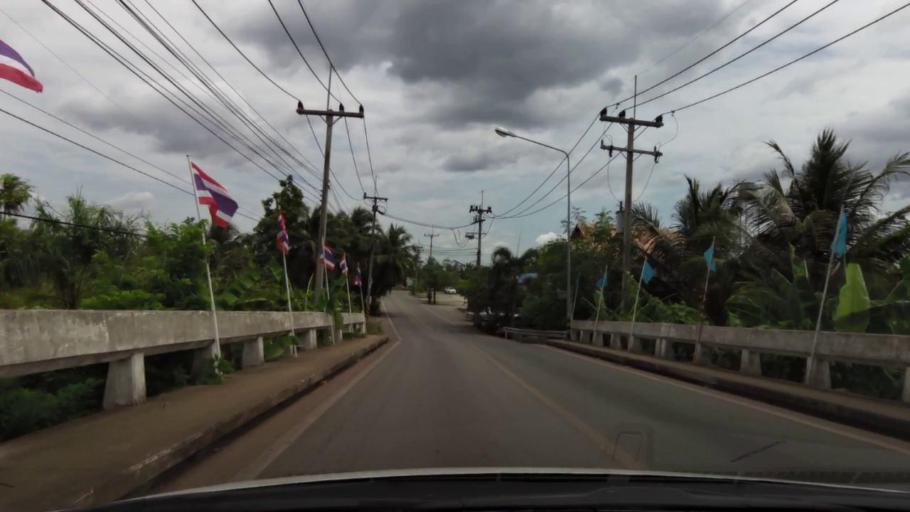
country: TH
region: Ratchaburi
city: Damnoen Saduak
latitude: 13.5472
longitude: 100.0176
